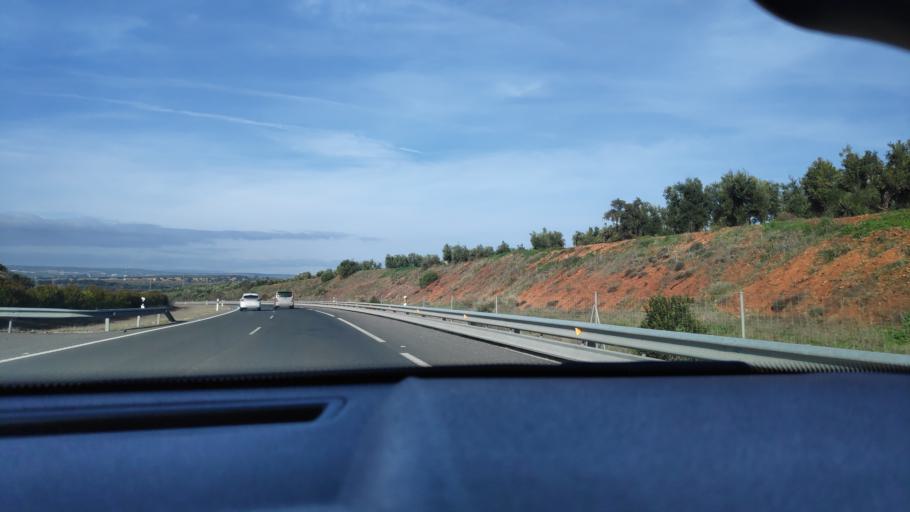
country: ES
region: Andalusia
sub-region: Provincia de Jaen
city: Bailen
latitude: 38.0972
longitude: -3.7098
